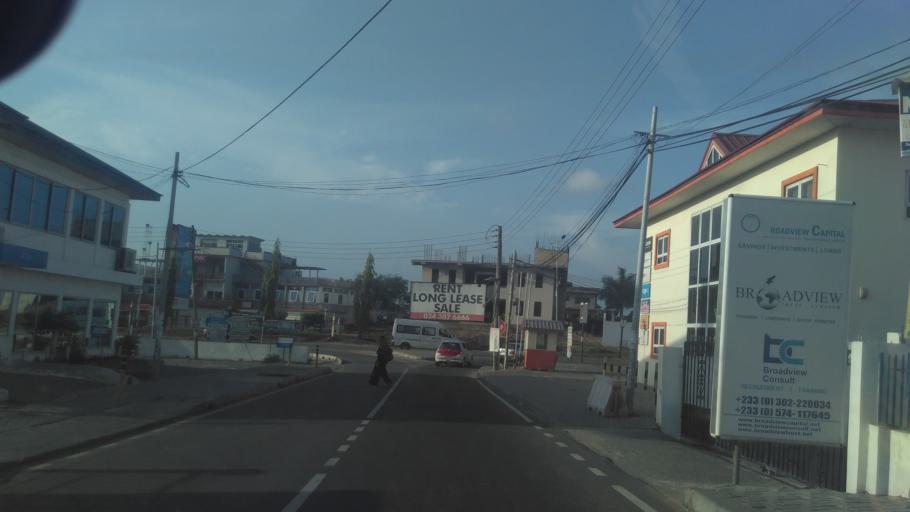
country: GH
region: Greater Accra
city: Accra
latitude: 5.5719
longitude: -0.2034
